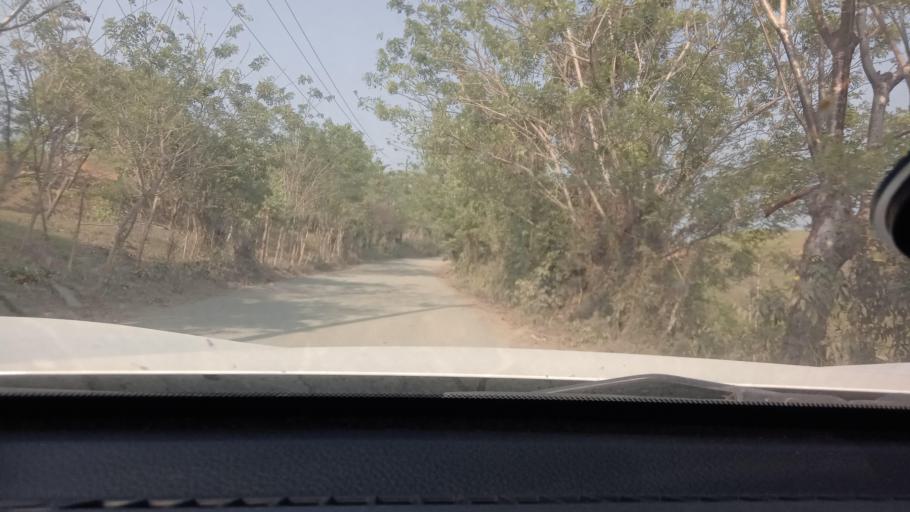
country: MX
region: Tabasco
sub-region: Huimanguillo
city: Francisco Rueda
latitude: 17.6537
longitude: -93.8959
